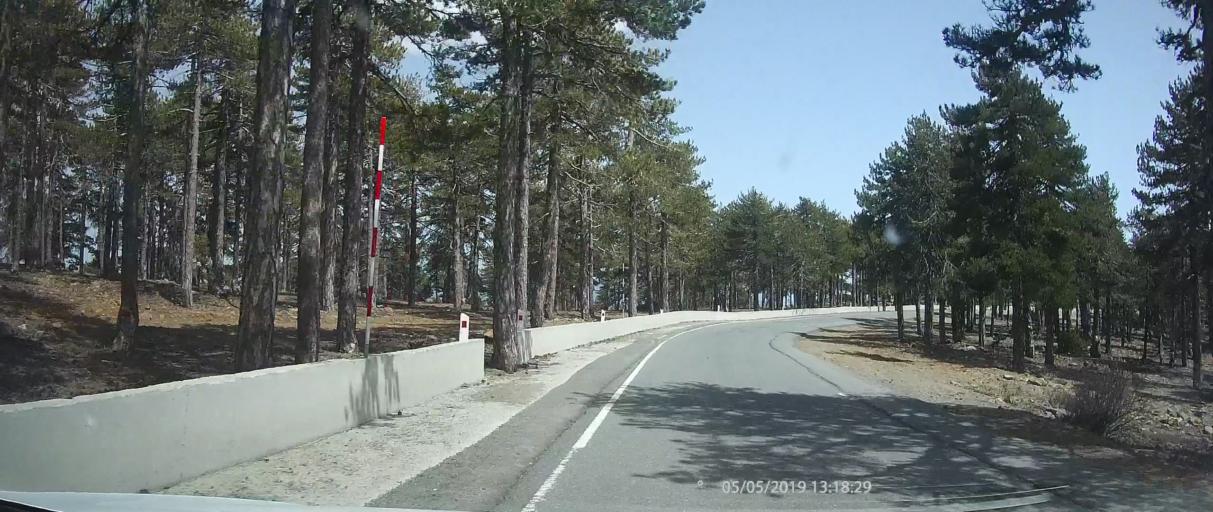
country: CY
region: Lefkosia
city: Kakopetria
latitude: 34.9343
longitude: 32.8680
